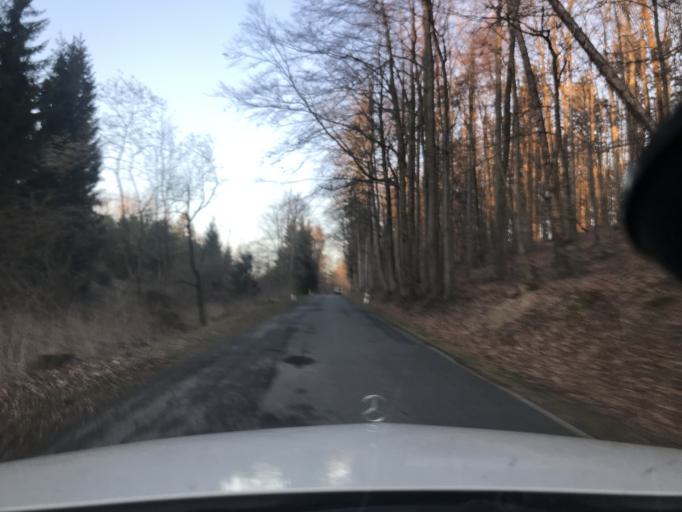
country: DE
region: Thuringia
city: Heyerode
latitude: 51.2006
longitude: 10.3103
